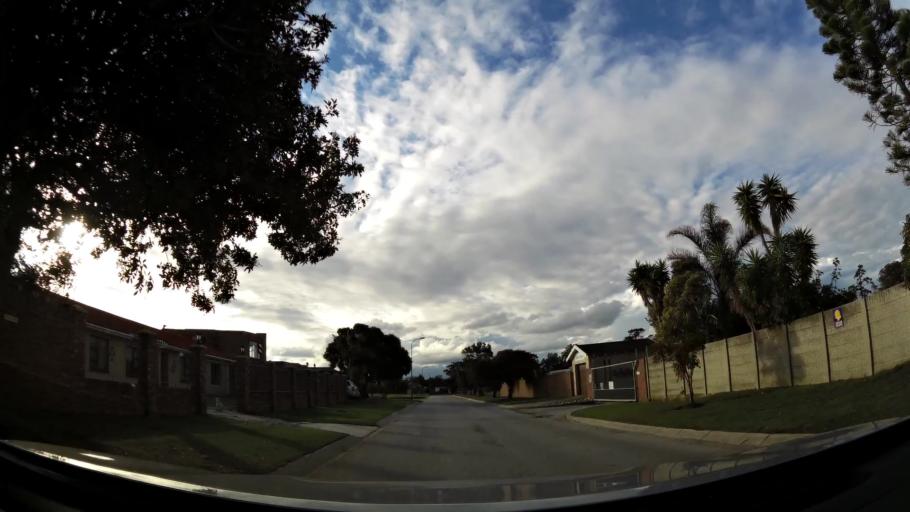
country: ZA
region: Eastern Cape
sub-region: Nelson Mandela Bay Metropolitan Municipality
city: Port Elizabeth
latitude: -33.9579
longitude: 25.4954
